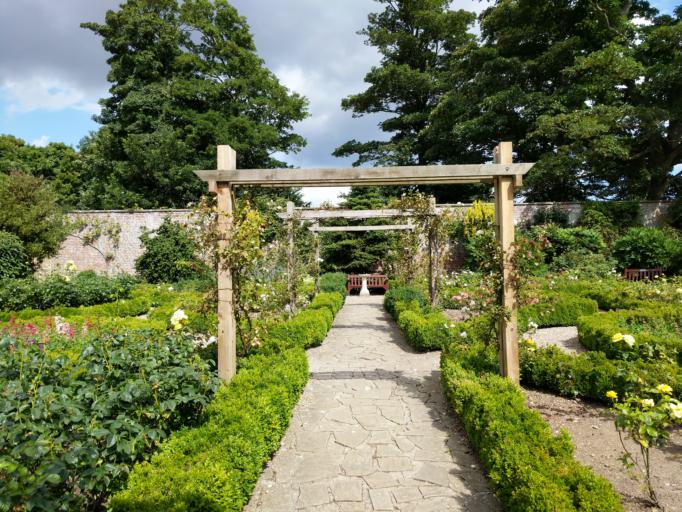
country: GB
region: England
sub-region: East Riding of Yorkshire
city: Bempton
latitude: 54.1043
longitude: -0.1578
